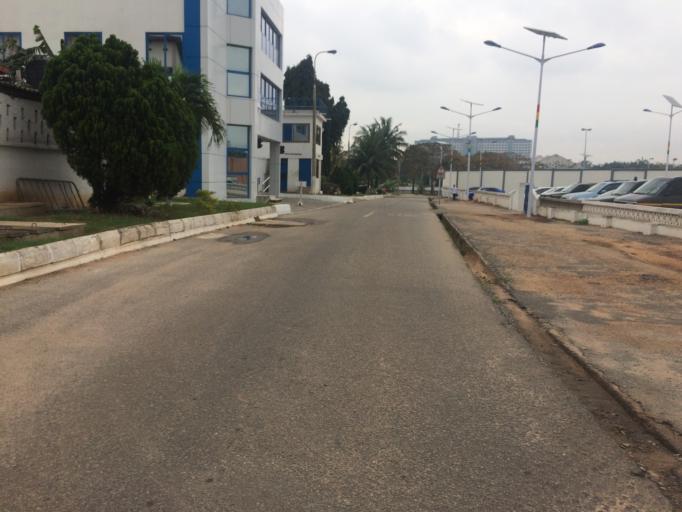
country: GH
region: Greater Accra
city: Accra
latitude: 5.5516
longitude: -0.1939
